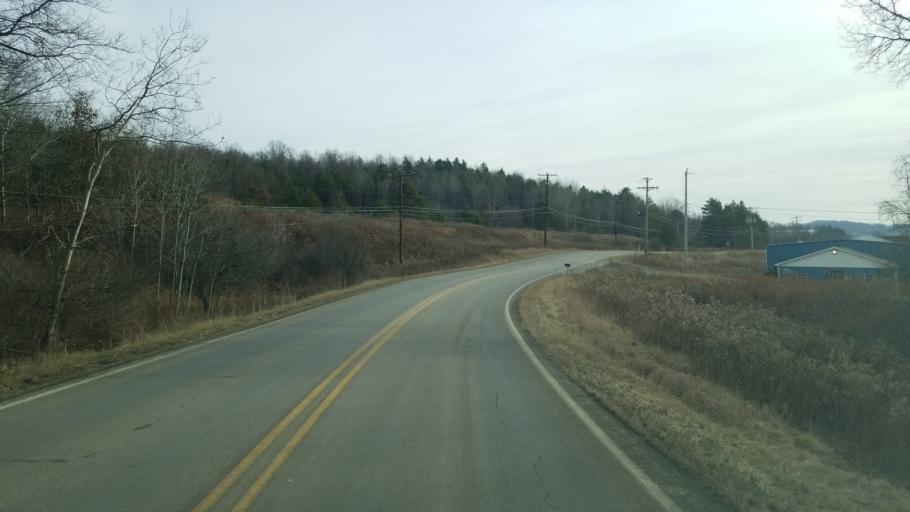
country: US
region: Pennsylvania
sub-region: Jefferson County
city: Punxsutawney
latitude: 40.9571
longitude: -78.9868
